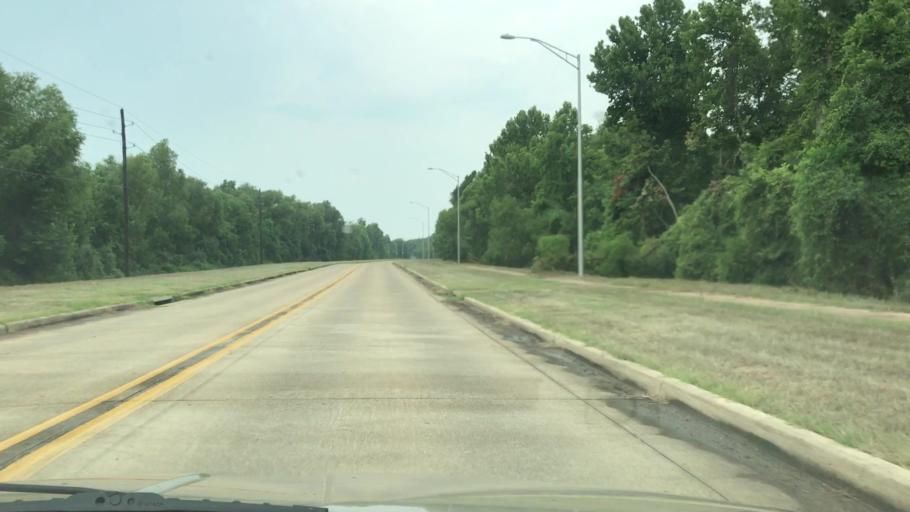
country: US
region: Louisiana
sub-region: Bossier Parish
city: Bossier City
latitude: 32.4739
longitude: -93.6965
